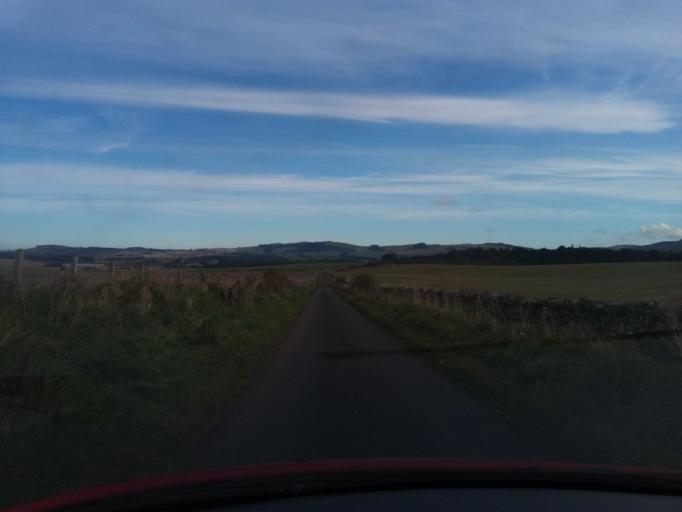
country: GB
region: Scotland
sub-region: The Scottish Borders
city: Kelso
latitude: 55.5101
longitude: -2.4045
